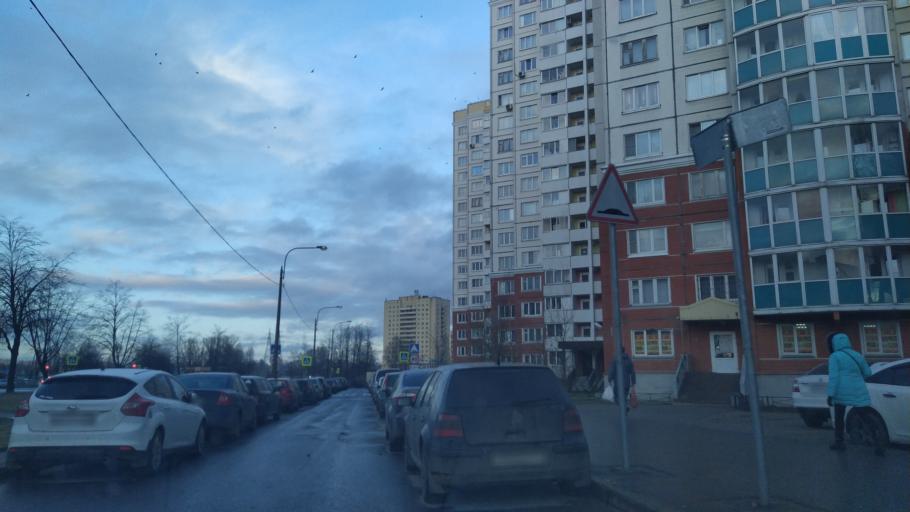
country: RU
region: St.-Petersburg
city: Grazhdanka
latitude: 60.0116
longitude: 30.4293
